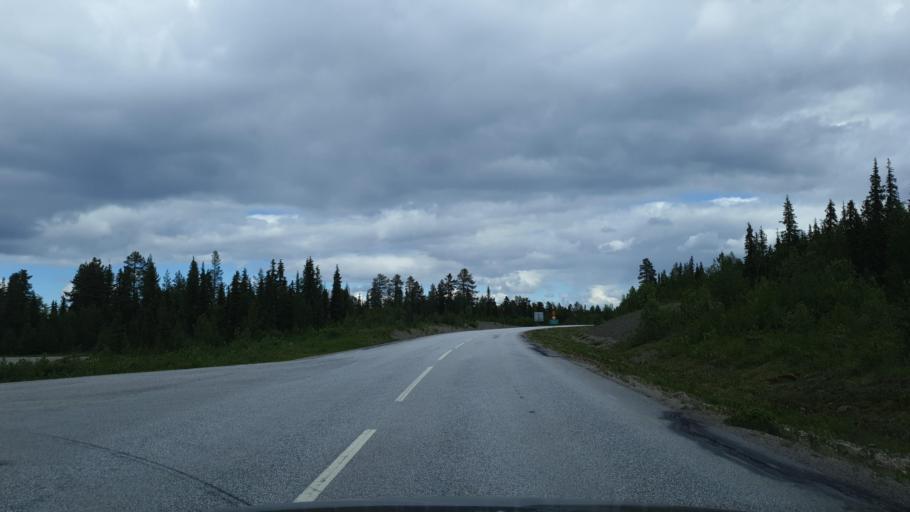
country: SE
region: Norrbotten
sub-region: Jokkmokks Kommun
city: Jokkmokk
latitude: 67.0176
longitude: 19.8591
